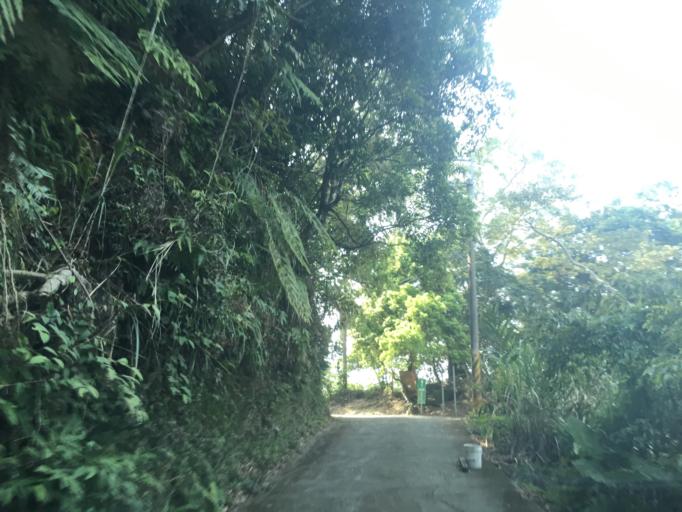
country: TW
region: Taiwan
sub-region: Taichung City
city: Taichung
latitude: 24.1397
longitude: 120.8211
